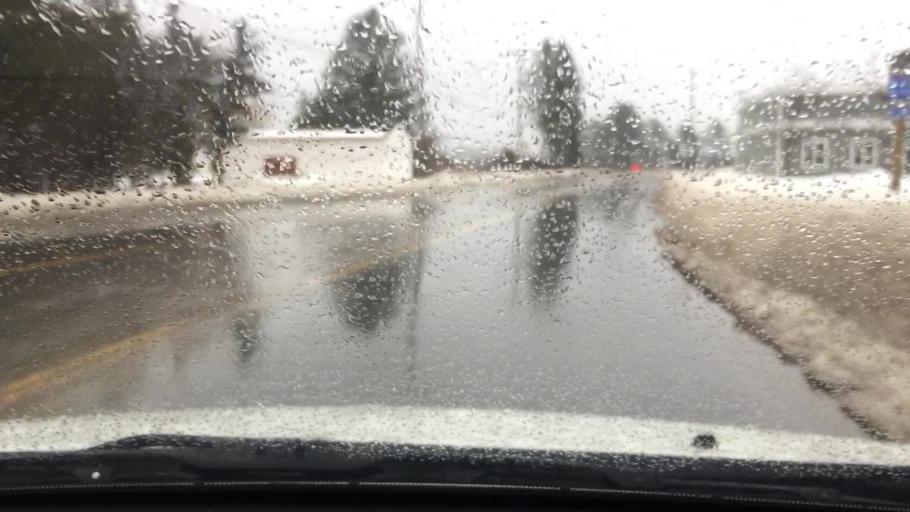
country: US
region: Michigan
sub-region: Charlevoix County
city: East Jordan
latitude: 45.1538
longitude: -85.1342
